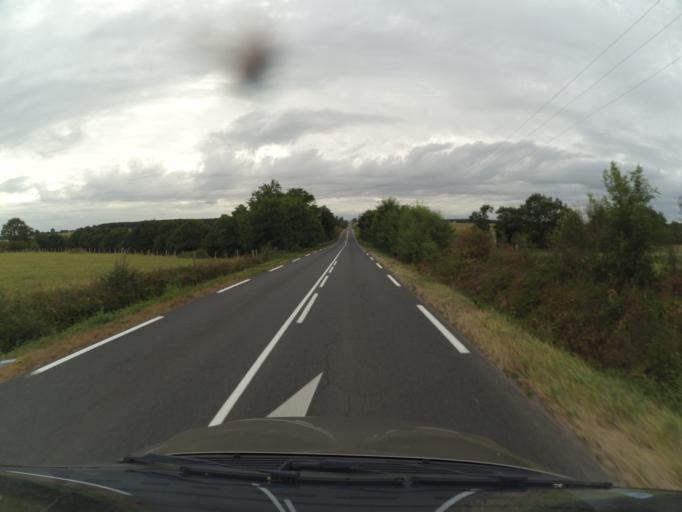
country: FR
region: Pays de la Loire
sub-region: Departement de Maine-et-Loire
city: Le Longeron
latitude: 47.0291
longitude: -1.0798
